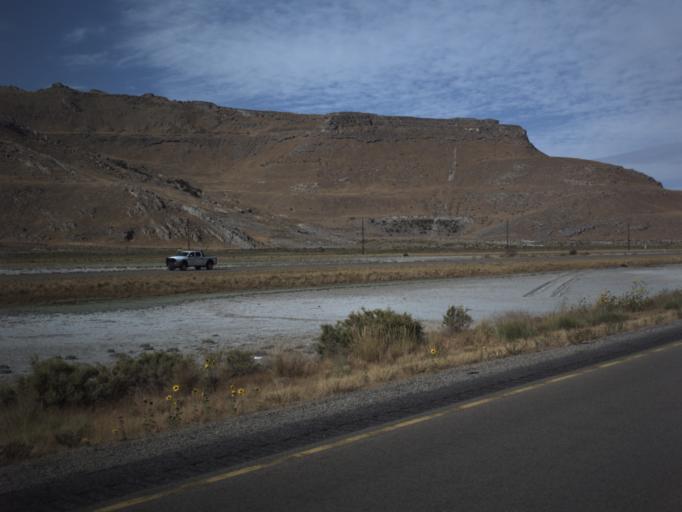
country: US
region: Utah
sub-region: Tooele County
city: Grantsville
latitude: 40.7399
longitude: -112.6211
